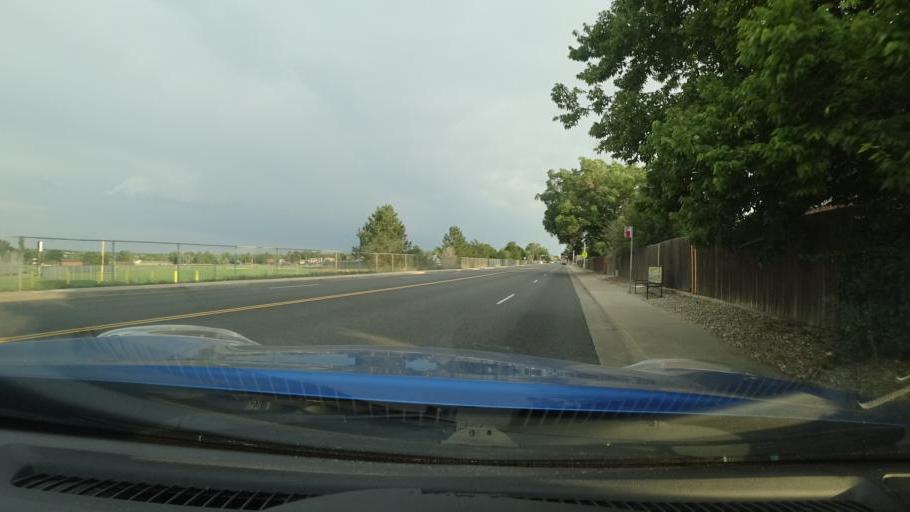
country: US
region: Colorado
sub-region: Adams County
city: Aurora
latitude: 39.6920
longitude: -104.8193
